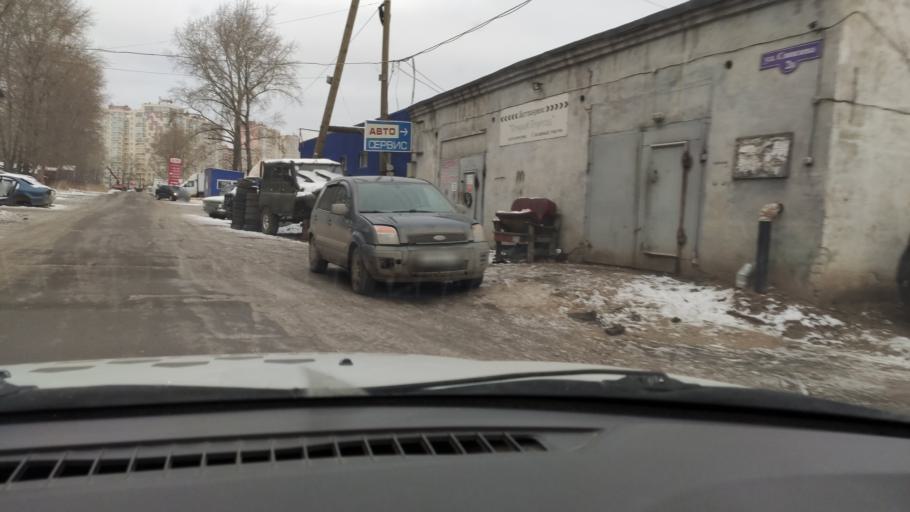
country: RU
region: Perm
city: Perm
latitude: 57.9645
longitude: 56.2033
